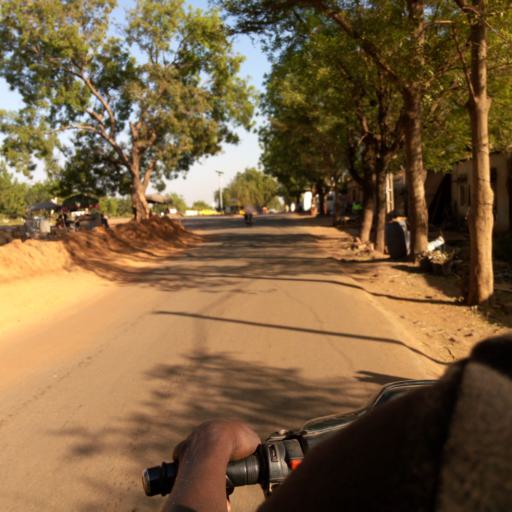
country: ML
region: Bamako
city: Bamako
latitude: 12.6567
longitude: -8.0276
